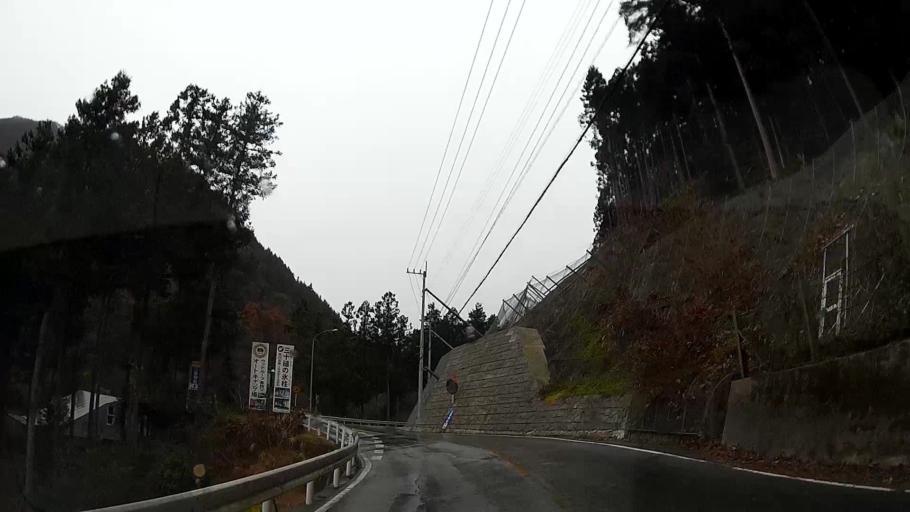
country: JP
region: Saitama
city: Chichibu
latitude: 35.9452
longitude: 138.9269
